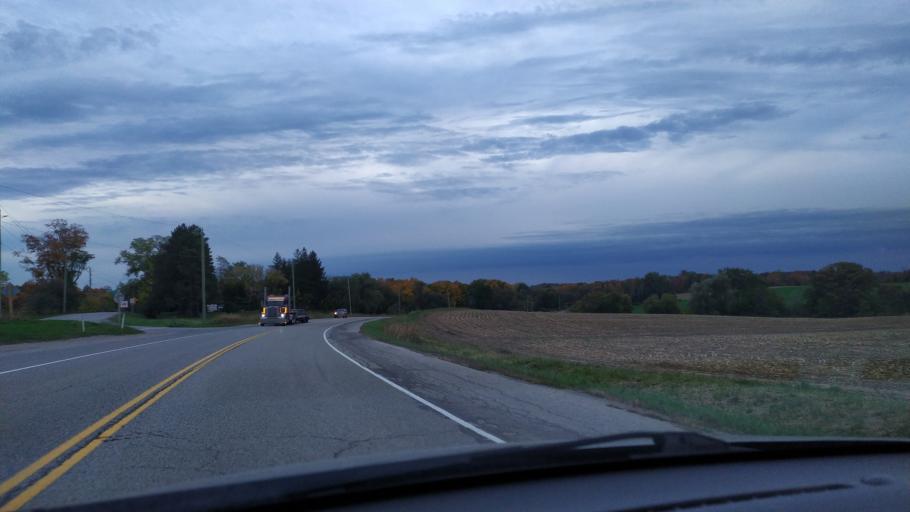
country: CA
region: Ontario
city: Stratford
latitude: 43.4734
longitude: -80.7837
